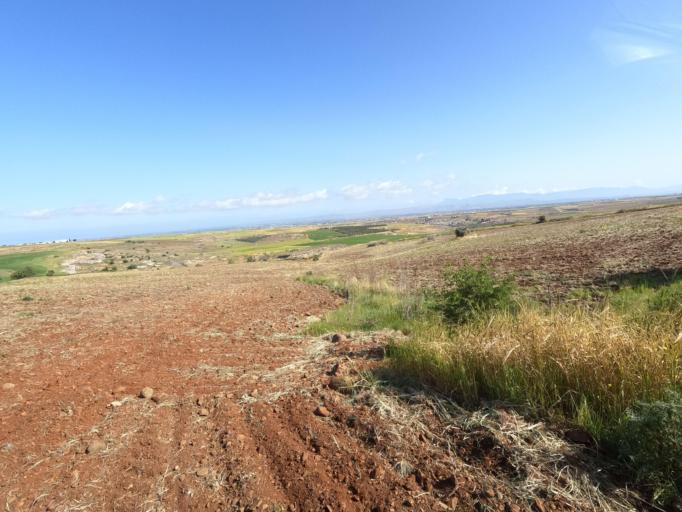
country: CY
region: Lefkosia
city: Astromeritis
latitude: 35.0862
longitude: 33.0226
